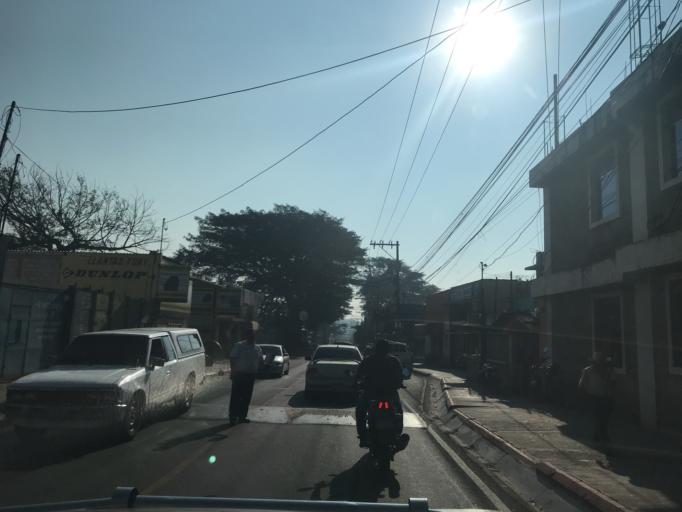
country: GT
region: Guatemala
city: Amatitlan
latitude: 14.4884
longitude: -90.6234
